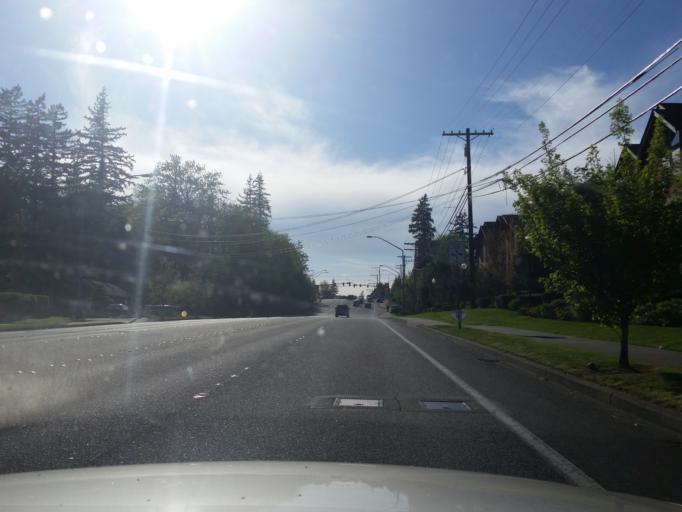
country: US
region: Washington
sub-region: Snohomish County
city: Alderwood Manor
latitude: 47.8501
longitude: -122.2776
